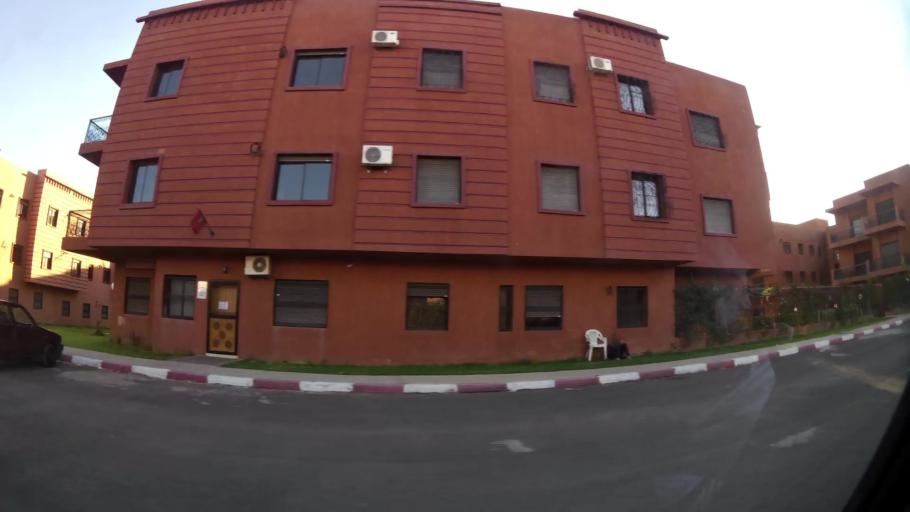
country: MA
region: Marrakech-Tensift-Al Haouz
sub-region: Marrakech
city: Marrakesh
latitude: 31.7490
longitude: -8.1092
